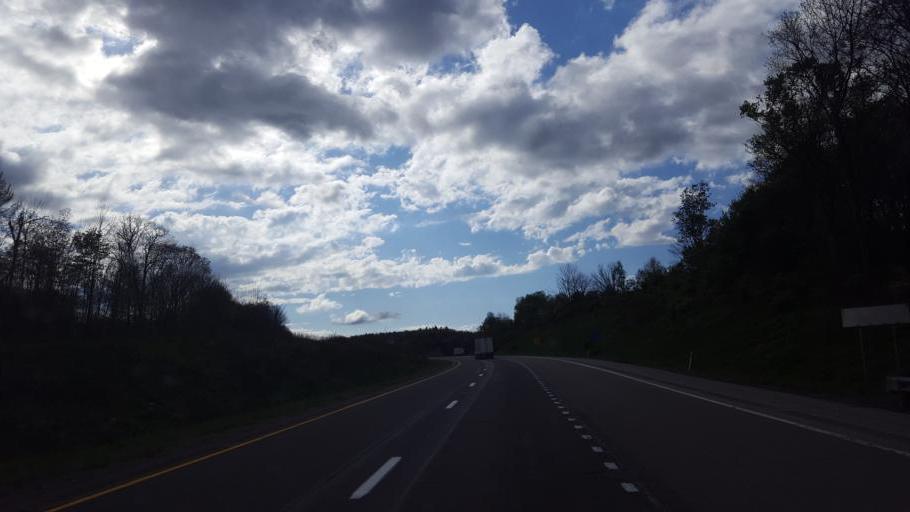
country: US
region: Pennsylvania
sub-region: Clarion County
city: Knox
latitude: 41.1736
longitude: -79.7325
